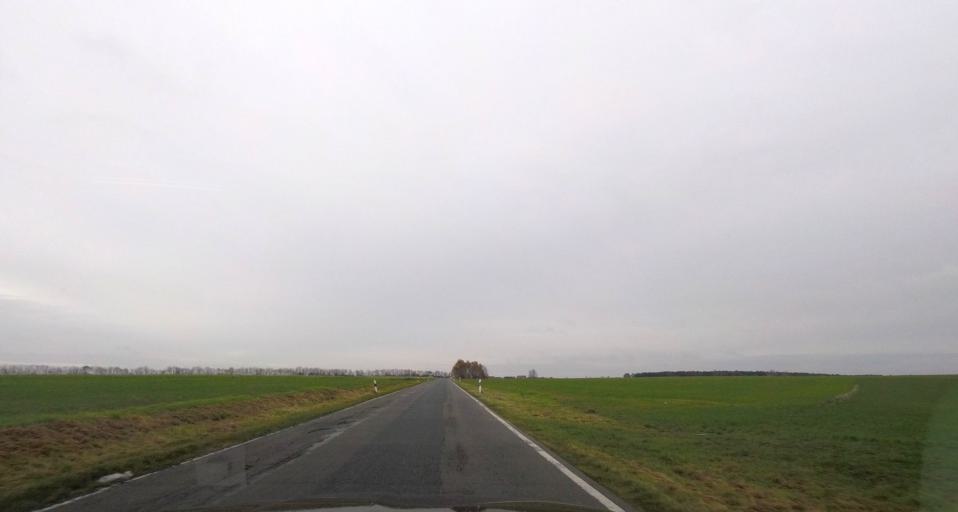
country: DE
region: Saxony-Anhalt
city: Kropstadt
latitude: 51.9812
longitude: 12.8153
